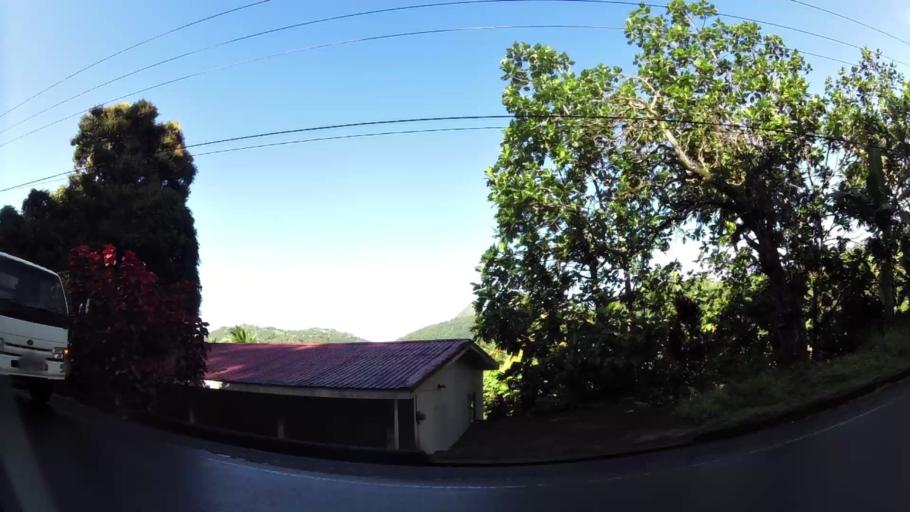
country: LC
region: Soufriere
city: Soufriere
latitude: 13.8164
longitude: -61.0376
